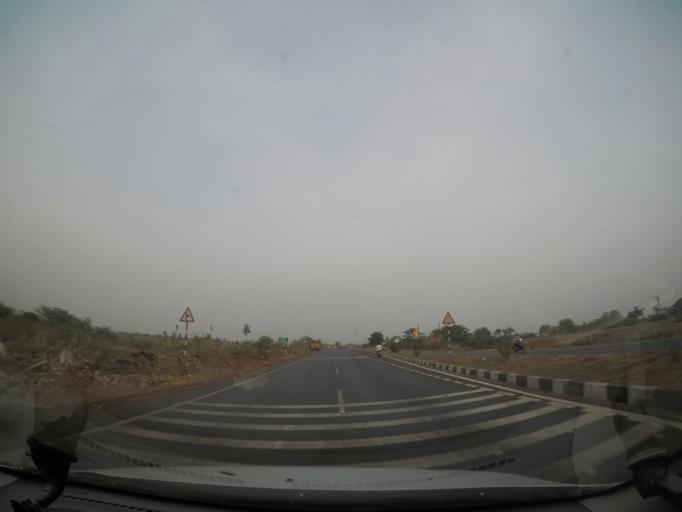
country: IN
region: Andhra Pradesh
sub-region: Krishna
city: Gannavaram
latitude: 16.6310
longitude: 80.9494
